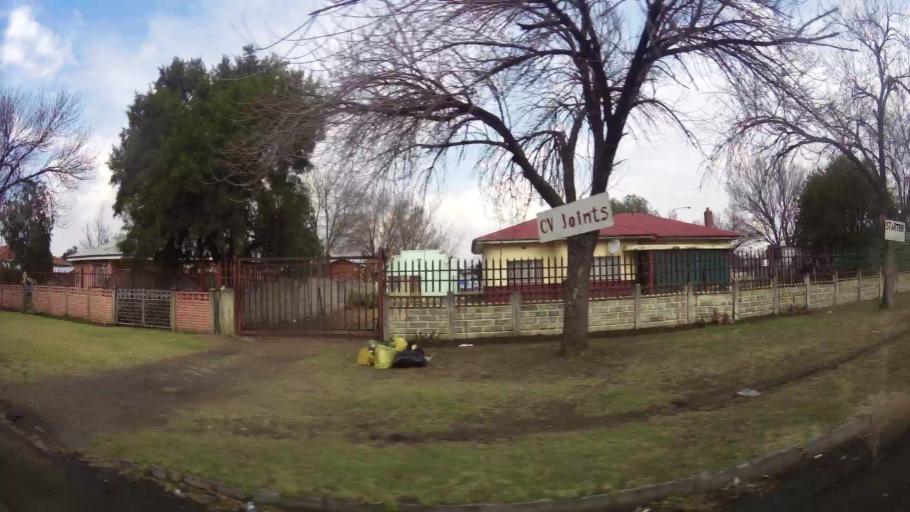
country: ZA
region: Gauteng
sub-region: Sedibeng District Municipality
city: Vereeniging
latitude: -26.6782
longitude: 27.9180
